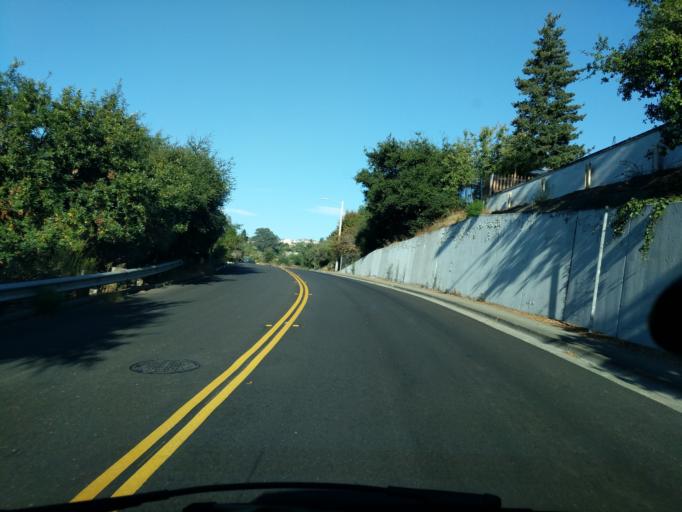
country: US
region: California
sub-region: Alameda County
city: Fairview
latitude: 37.6541
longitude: -122.0297
